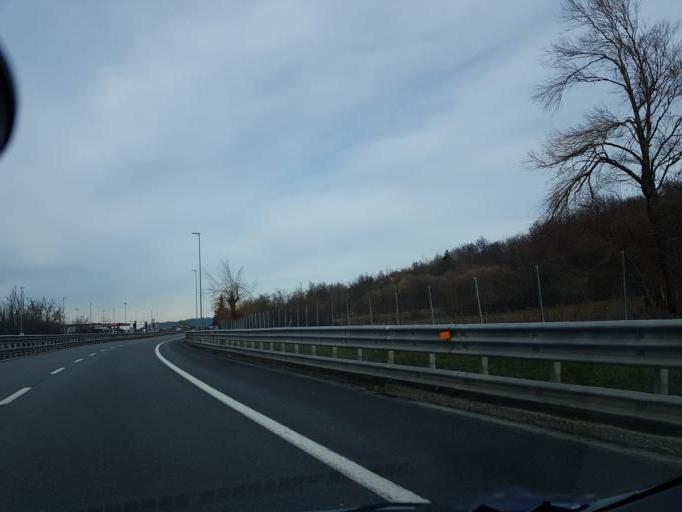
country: IT
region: Piedmont
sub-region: Provincia di Alessandria
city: Arquata Scrivia
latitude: 44.6680
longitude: 8.9080
